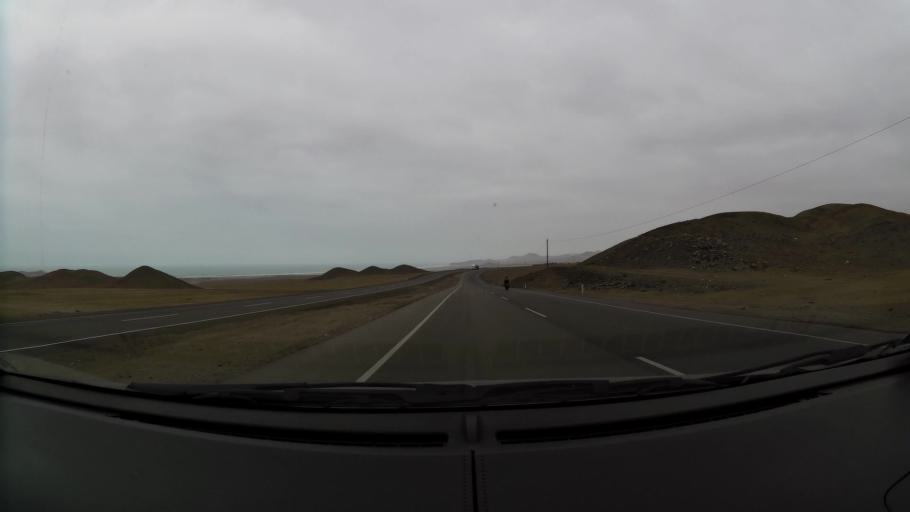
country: PE
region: Lima
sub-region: Barranca
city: Paramonga
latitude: -10.5583
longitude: -77.8798
